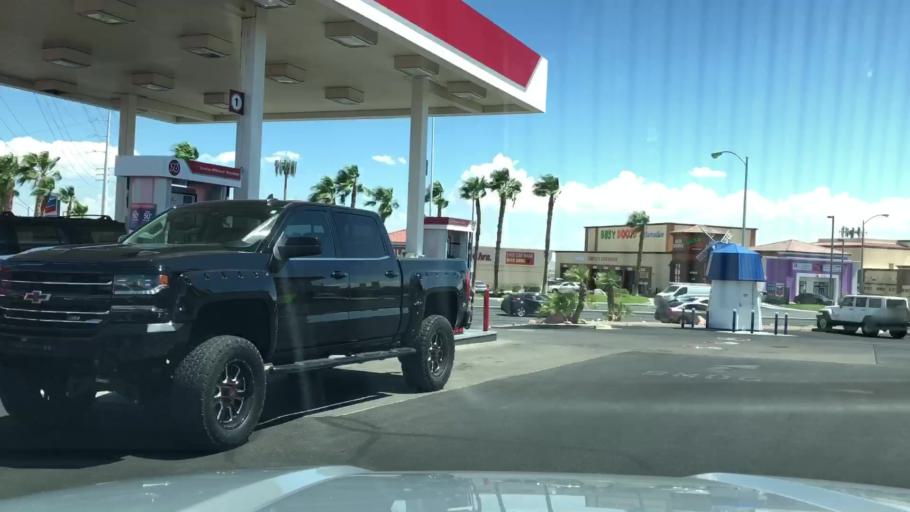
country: US
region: Nevada
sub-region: Clark County
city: Spring Valley
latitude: 36.1146
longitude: -115.2797
